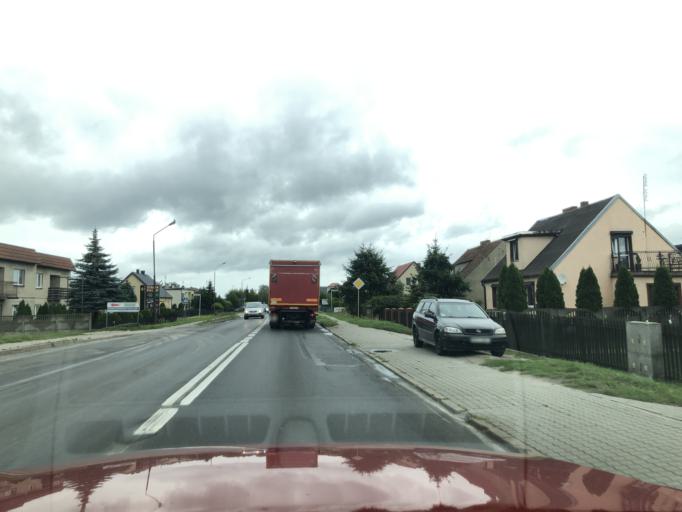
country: PL
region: Greater Poland Voivodeship
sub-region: Powiat szamotulski
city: Wronki
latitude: 52.7011
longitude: 16.3869
